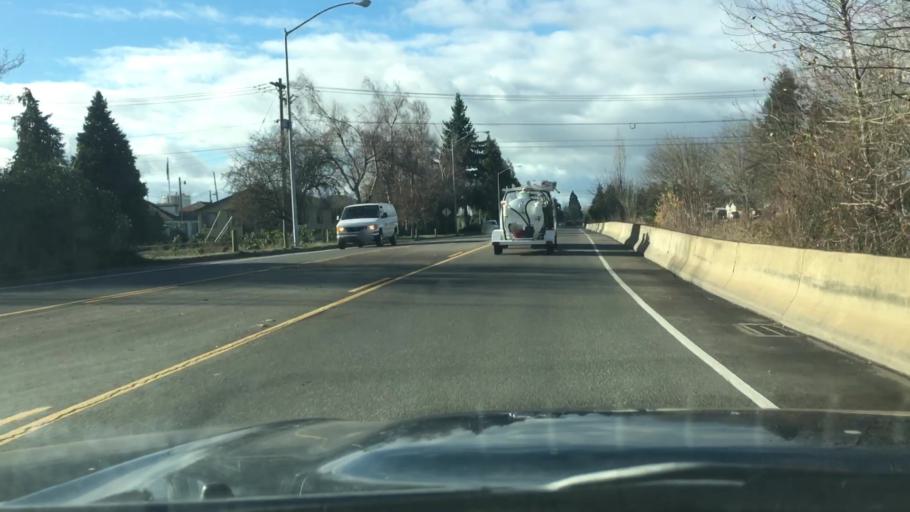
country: US
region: Oregon
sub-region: Lane County
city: Eugene
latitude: 44.0632
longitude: -123.1502
